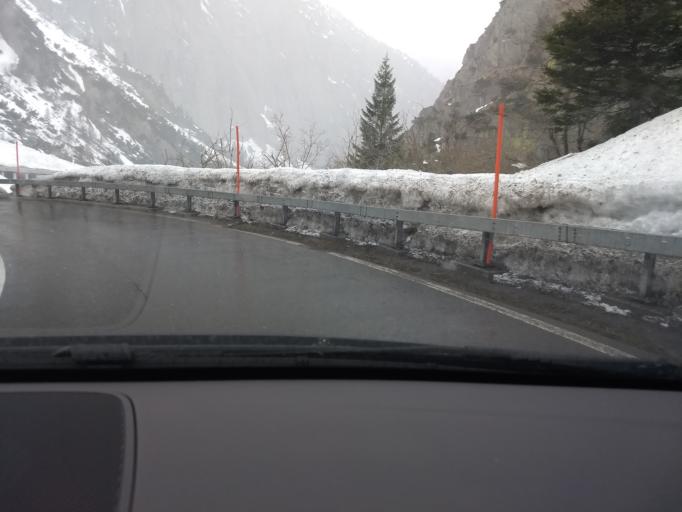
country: CH
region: Uri
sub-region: Uri
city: Andermatt
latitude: 46.6497
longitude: 8.5876
